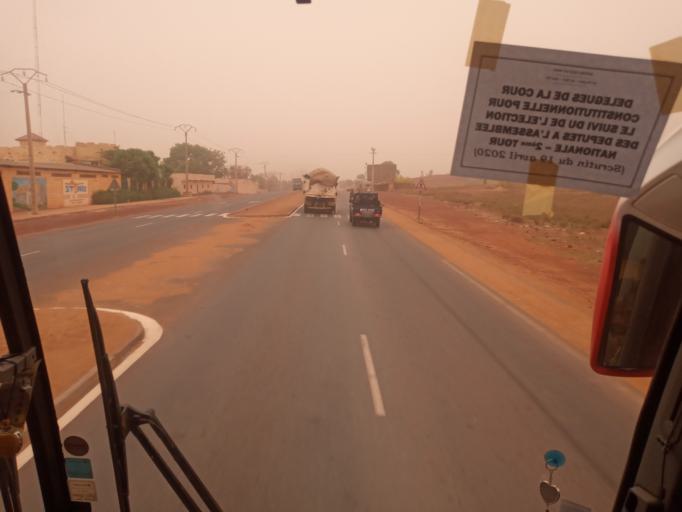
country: ML
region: Bamako
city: Bamako
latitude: 12.6813
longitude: -7.8014
